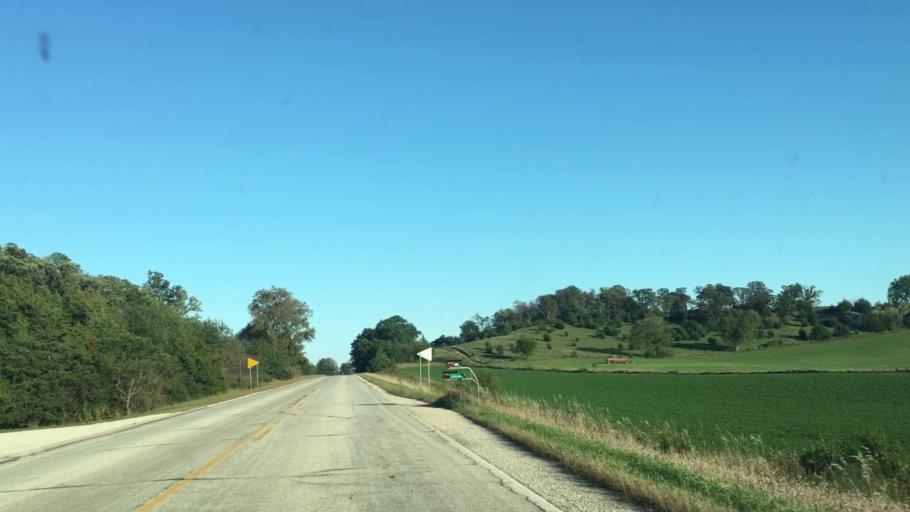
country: US
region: Minnesota
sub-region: Fillmore County
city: Chatfield
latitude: 43.8411
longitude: -92.0846
